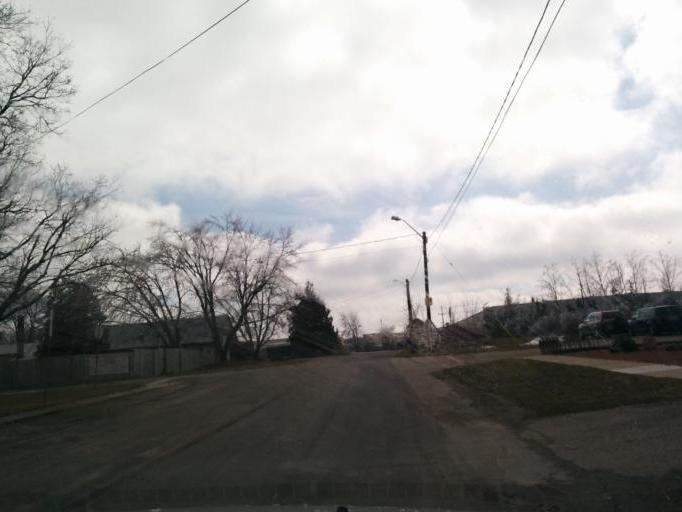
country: CA
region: Ontario
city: Waterloo
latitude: 43.5384
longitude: -80.5563
